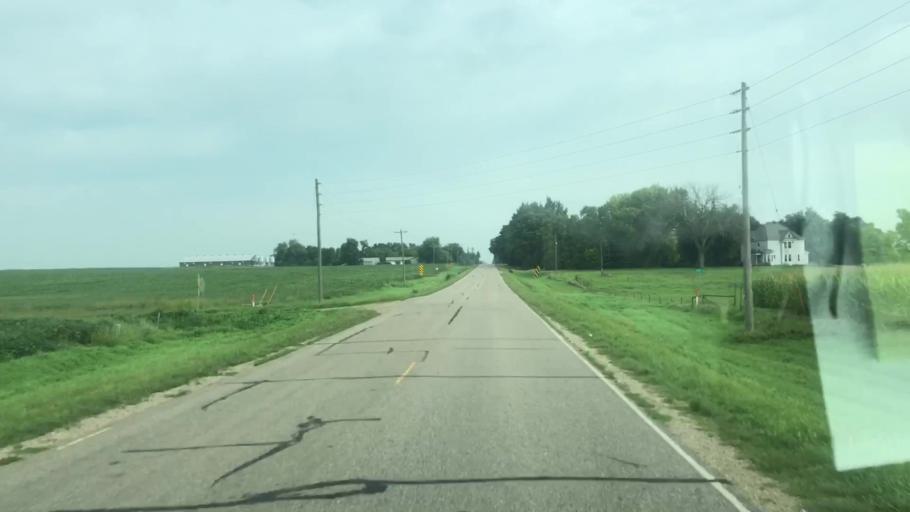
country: US
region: Iowa
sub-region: O'Brien County
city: Sheldon
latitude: 43.1998
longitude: -95.8622
